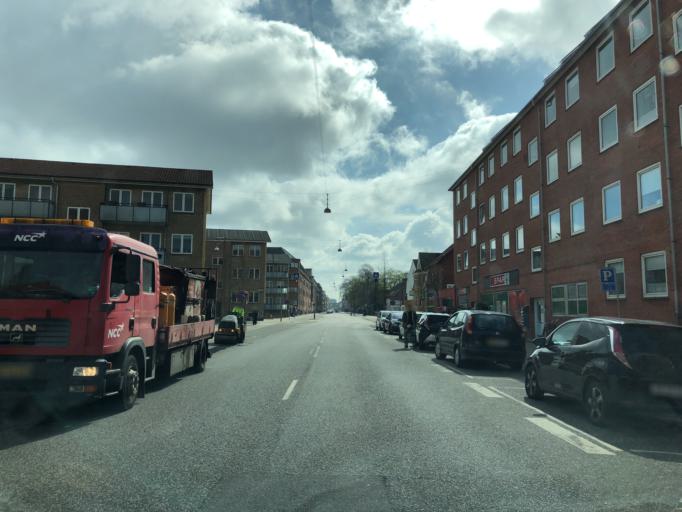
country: DK
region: North Denmark
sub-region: Alborg Kommune
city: Aalborg
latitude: 57.0553
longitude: 9.8953
